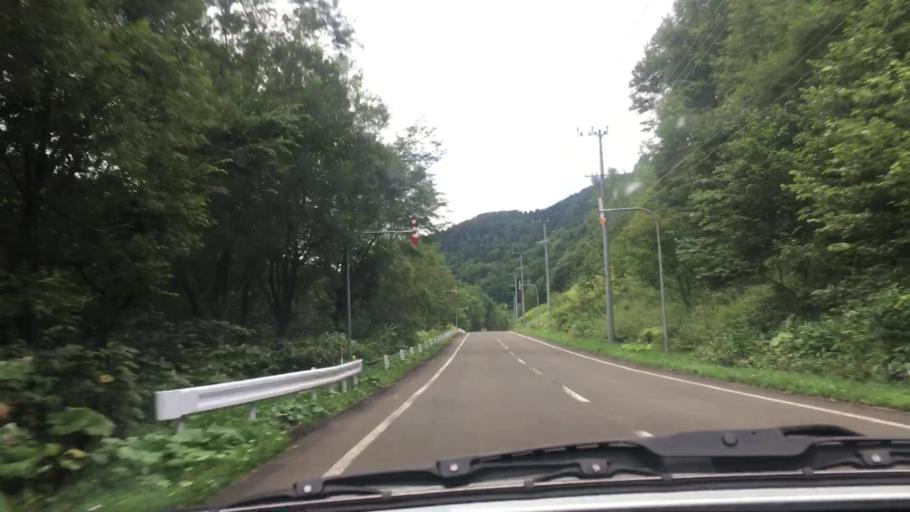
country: JP
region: Hokkaido
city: Shimo-furano
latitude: 43.0452
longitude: 142.5171
